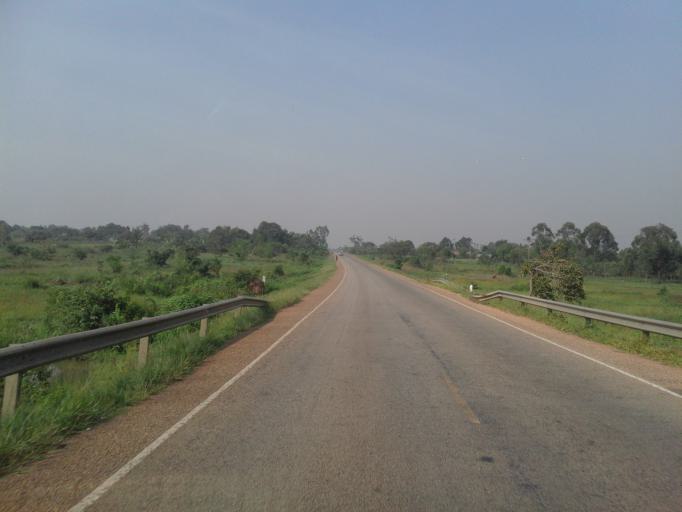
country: UG
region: Eastern Region
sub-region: Budaka District
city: Budaka
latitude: 1.0330
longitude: 33.9921
